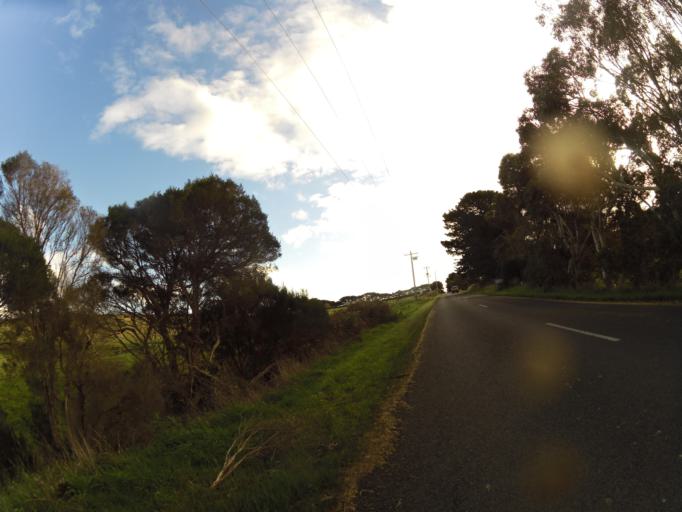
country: AU
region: Victoria
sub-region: Bass Coast
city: North Wonthaggi
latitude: -38.5480
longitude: 145.5599
